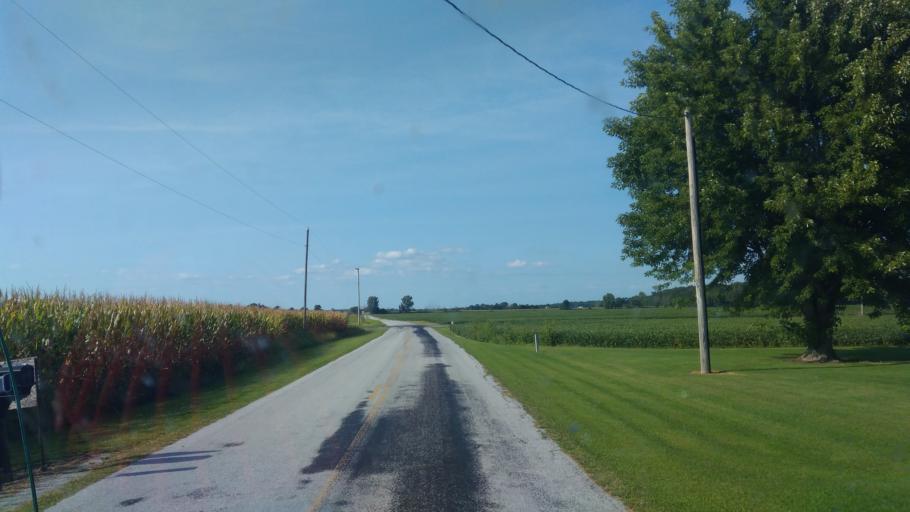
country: US
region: Ohio
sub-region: Hardin County
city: Kenton
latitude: 40.7233
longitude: -83.5725
